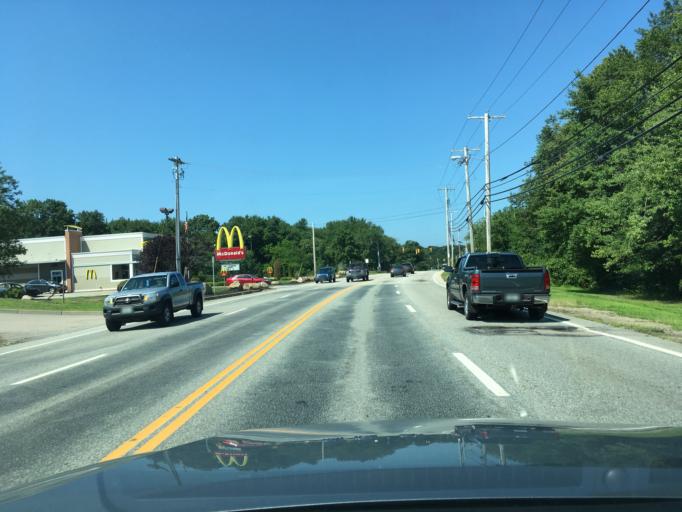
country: US
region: Rhode Island
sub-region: Kent County
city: West Warwick
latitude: 41.6792
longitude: -71.5791
